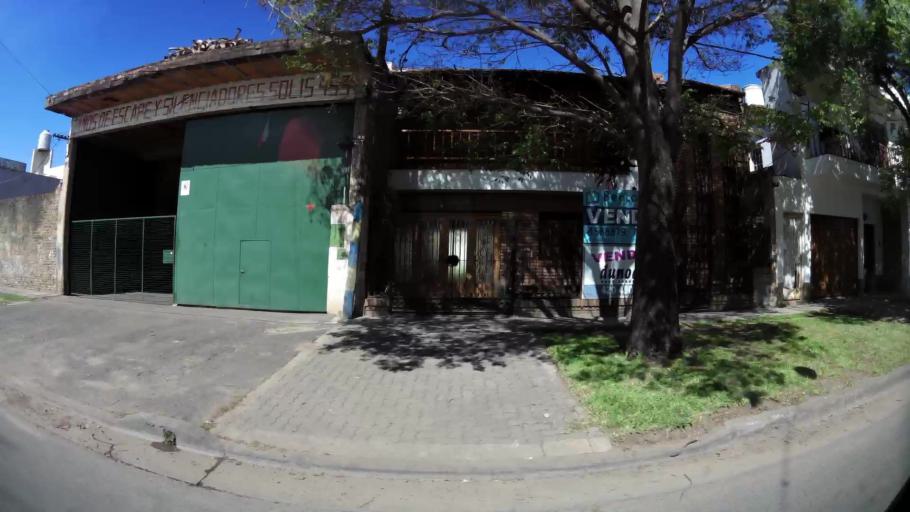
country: AR
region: Santa Fe
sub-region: Departamento de Rosario
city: Rosario
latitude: -32.9329
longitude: -60.7037
